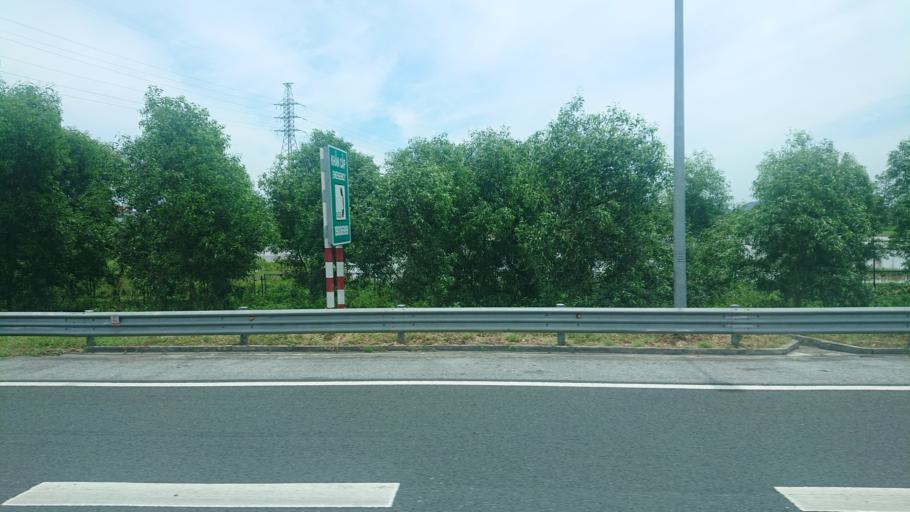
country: VN
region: Hai Phong
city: An Lao
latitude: 20.8019
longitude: 106.5293
